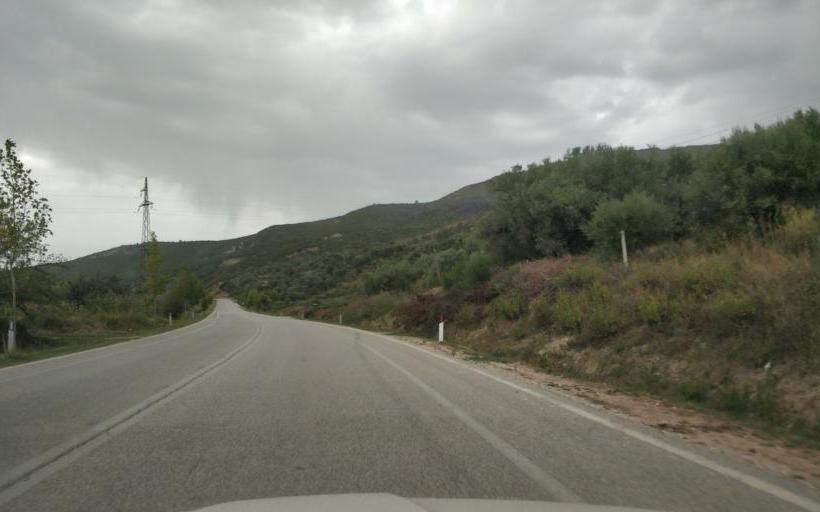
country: AL
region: Fier
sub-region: Rrethi i Mallakastres
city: Hekal
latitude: 40.5200
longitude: 19.7417
